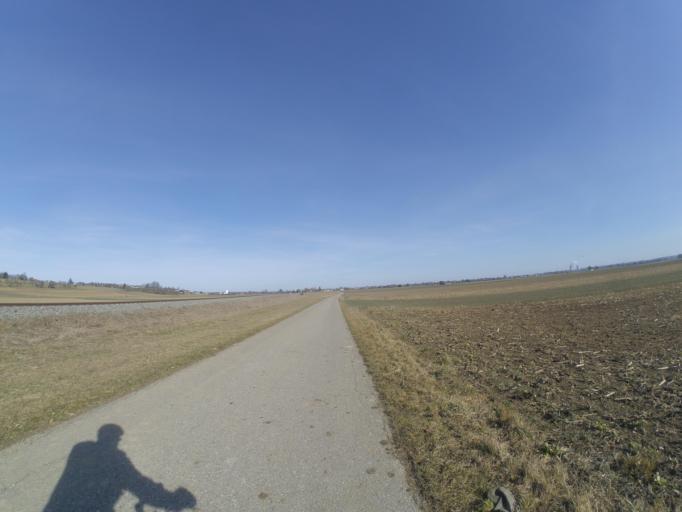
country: DE
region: Baden-Wuerttemberg
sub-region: Regierungsbezirk Stuttgart
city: Sontheim an der Brenz
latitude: 48.5439
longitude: 10.2714
